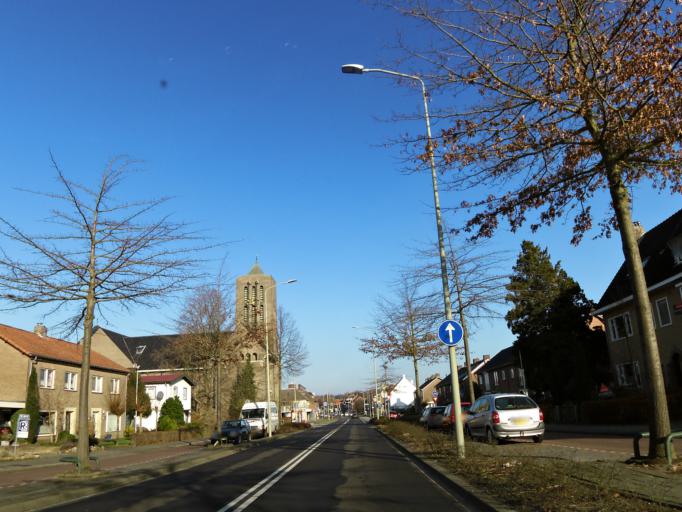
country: NL
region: Limburg
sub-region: Gemeente Heerlen
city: Heerlen
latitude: 50.9121
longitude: 5.9738
